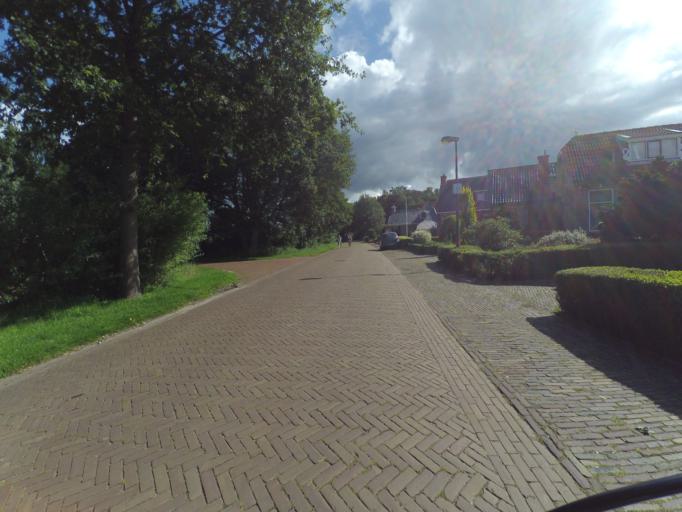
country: NL
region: Friesland
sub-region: Gemeente Tytsjerksteradiel
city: Sumar
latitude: 53.1965
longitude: 6.0032
